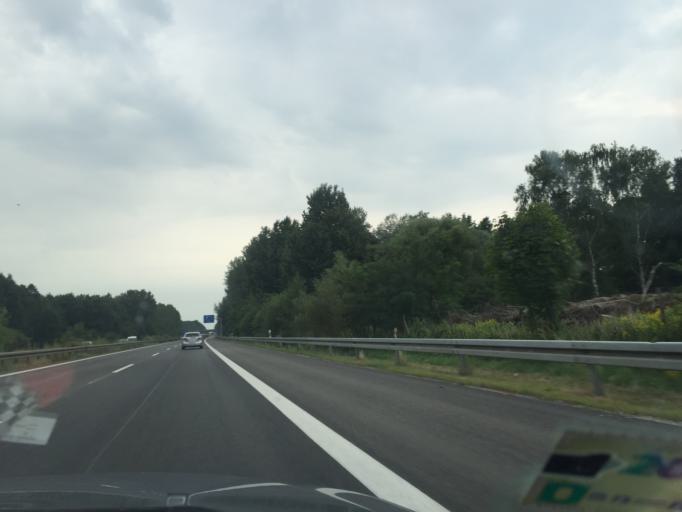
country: DE
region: Brandenburg
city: Bernau bei Berlin
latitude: 52.6576
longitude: 13.5693
